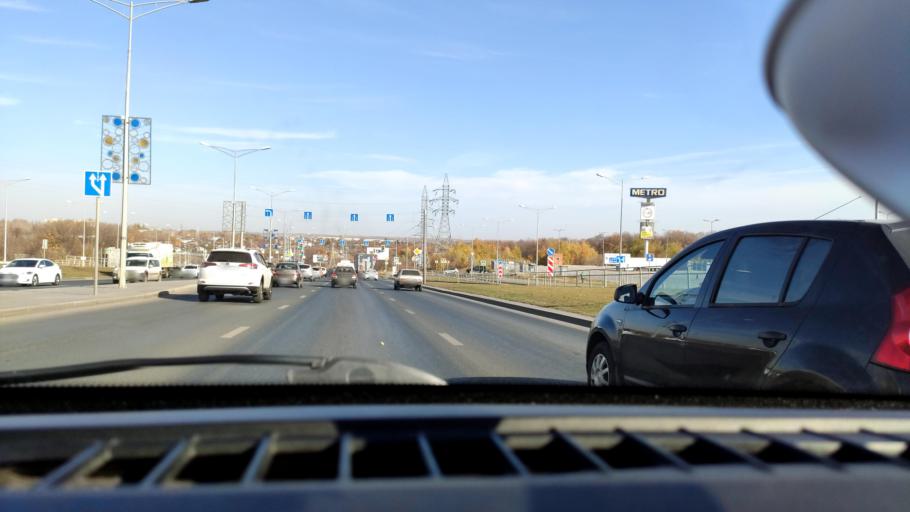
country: RU
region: Samara
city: Petra-Dubrava
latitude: 53.2791
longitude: 50.2744
